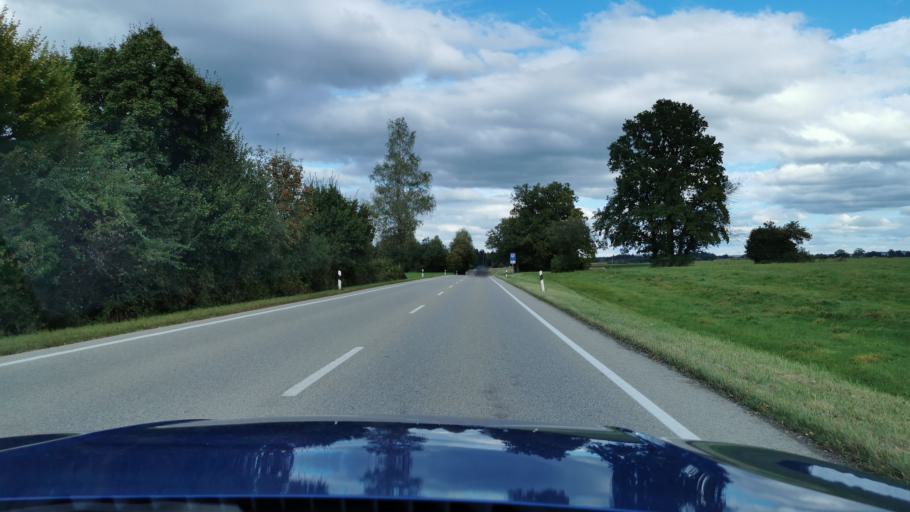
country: DE
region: Bavaria
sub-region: Upper Bavaria
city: Gaissach
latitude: 47.7653
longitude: 11.5878
